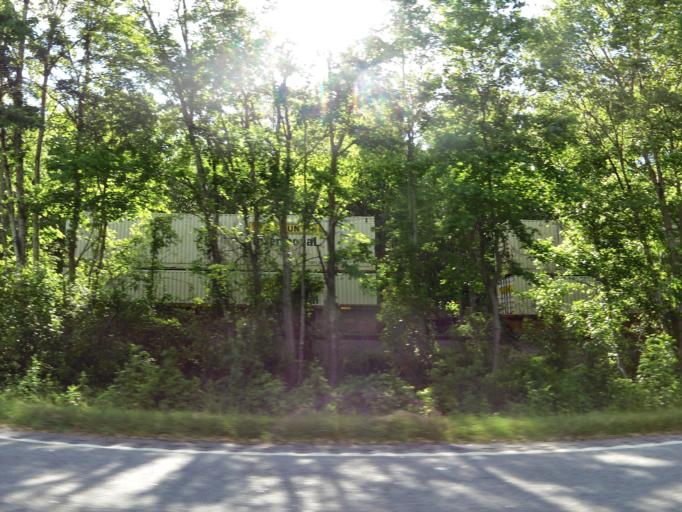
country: US
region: South Carolina
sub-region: Allendale County
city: Fairfax
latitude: 32.9150
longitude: -81.2375
